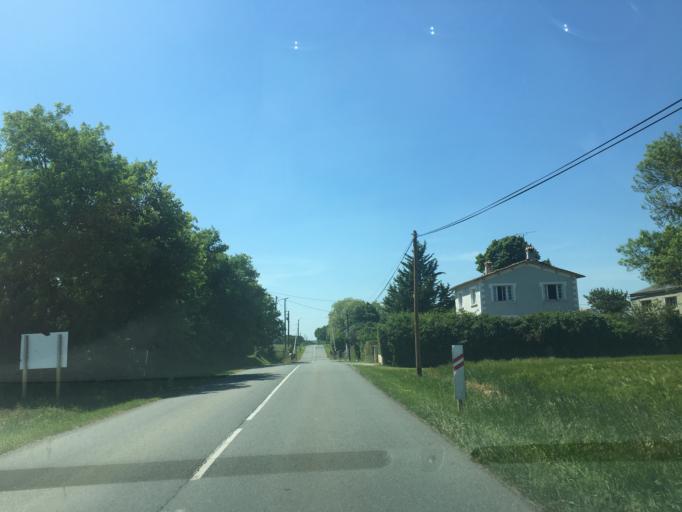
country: FR
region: Poitou-Charentes
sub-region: Departement des Deux-Sevres
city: Beauvoir-sur-Niort
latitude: 46.0757
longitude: -0.5158
